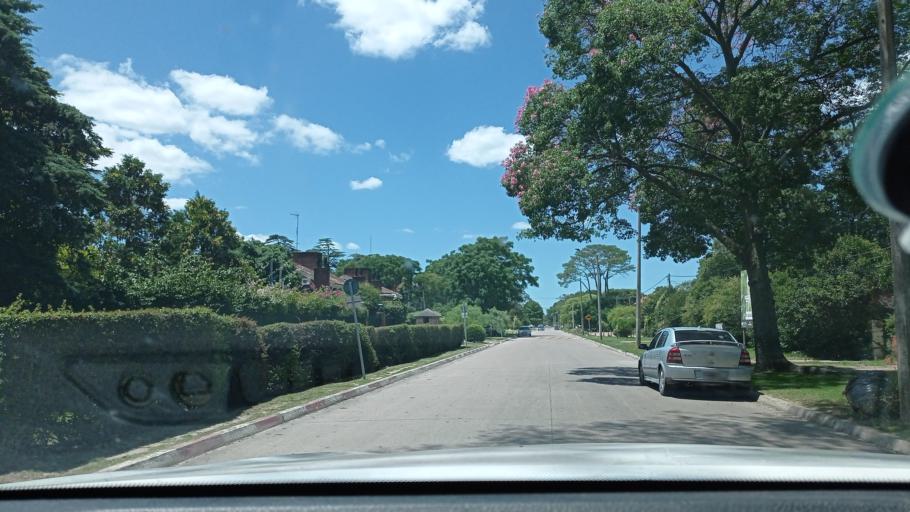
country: UY
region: Canelones
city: Paso de Carrasco
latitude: -34.8751
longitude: -56.0472
